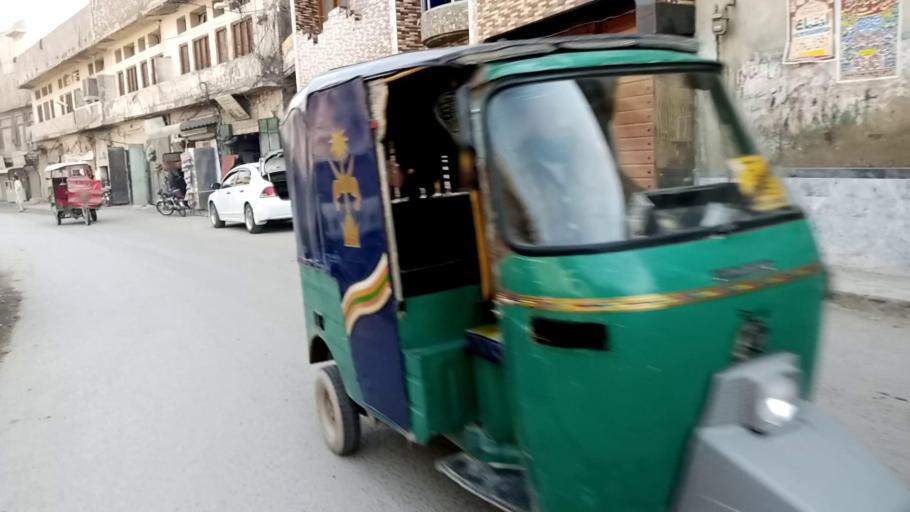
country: PK
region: Khyber Pakhtunkhwa
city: Peshawar
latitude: 33.9976
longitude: 71.5784
